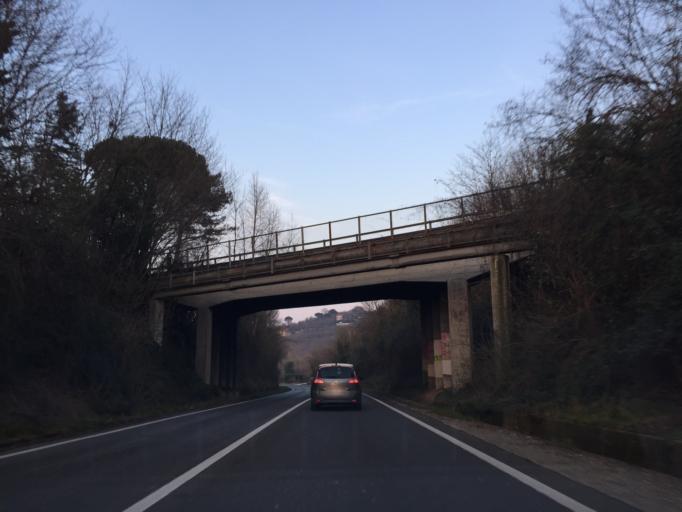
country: IT
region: Campania
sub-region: Provincia di Avellino
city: Avellino
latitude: 40.9025
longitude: 14.8050
